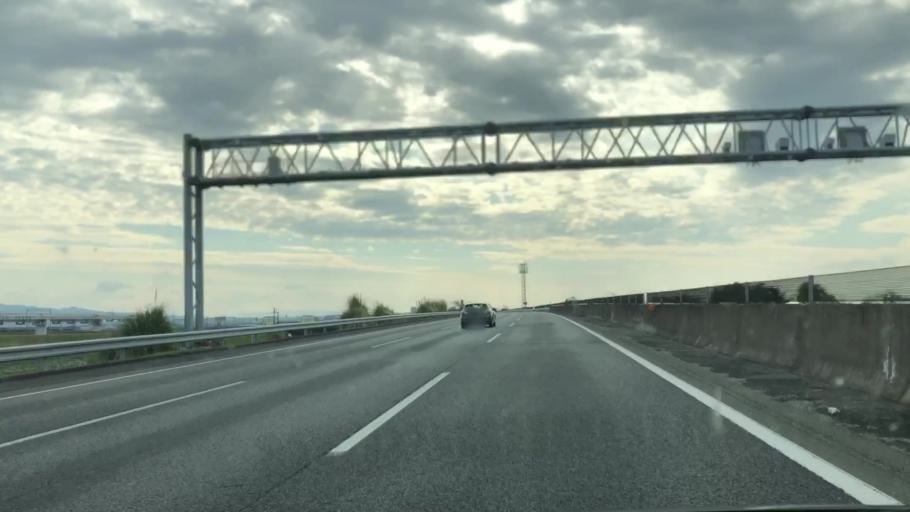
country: JP
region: Saga Prefecture
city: Tosu
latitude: 33.3567
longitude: 130.5389
